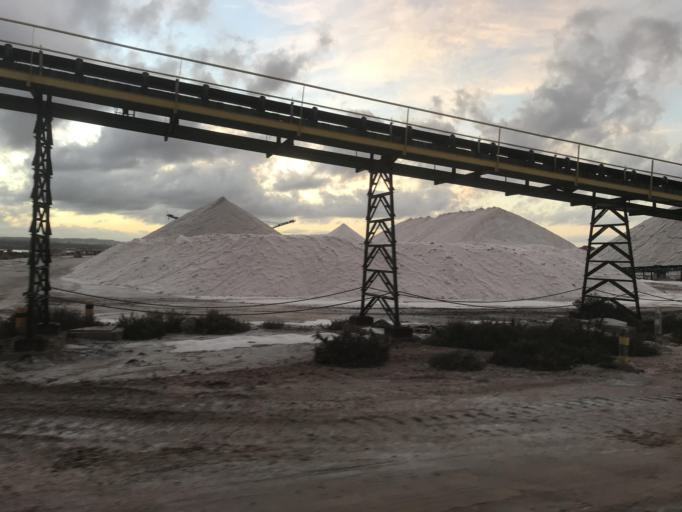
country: ES
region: Valencia
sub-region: Provincia de Alicante
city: Torrevieja
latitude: 37.9797
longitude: -0.6990
